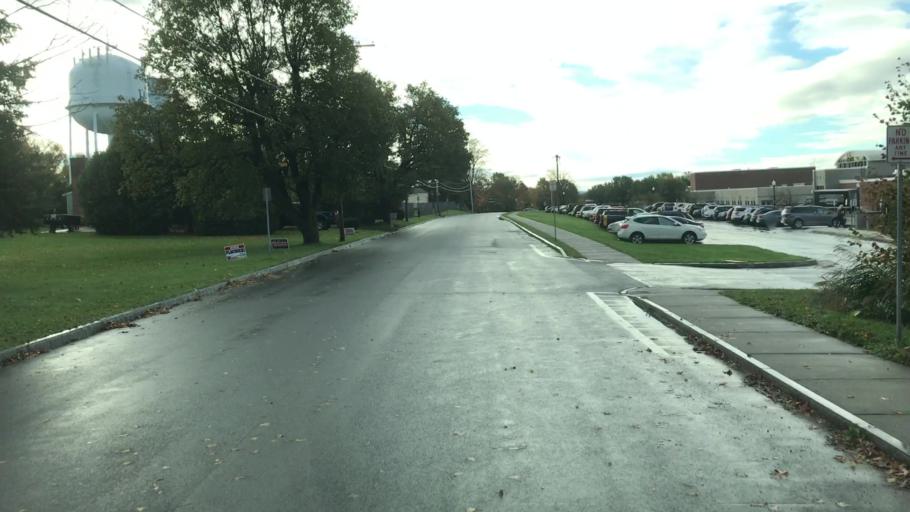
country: US
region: New York
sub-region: Onondaga County
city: Skaneateles
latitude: 42.9533
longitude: -76.4211
